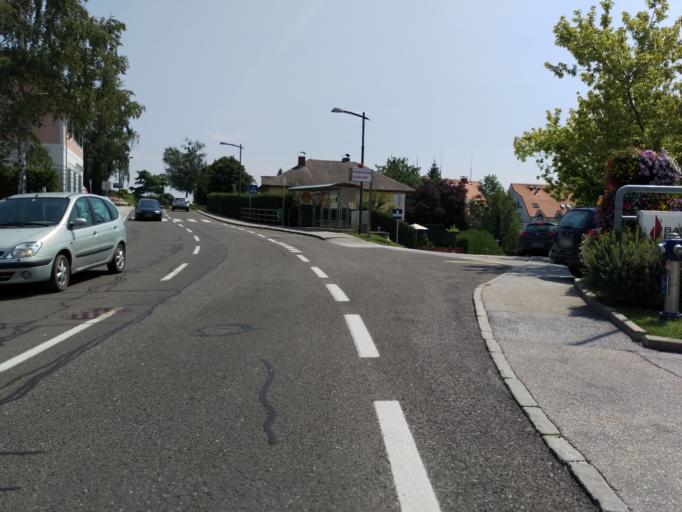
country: AT
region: Styria
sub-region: Politischer Bezirk Graz-Umgebung
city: Nestelbach bei Graz
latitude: 47.0750
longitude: 15.5897
